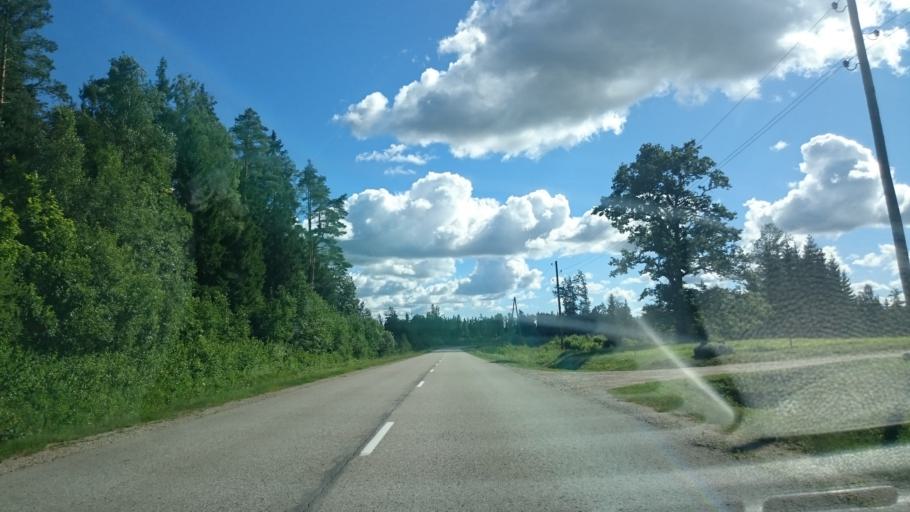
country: LV
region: Kuldigas Rajons
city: Kuldiga
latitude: 56.8835
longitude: 21.8781
